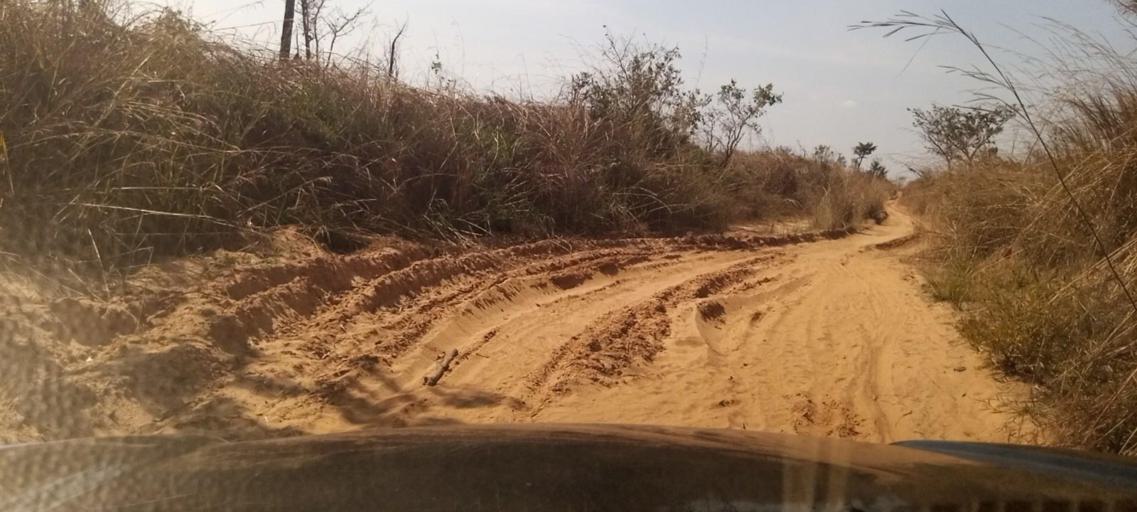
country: CD
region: Kasai-Oriental
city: Kabinda
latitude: -5.7787
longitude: 25.0671
